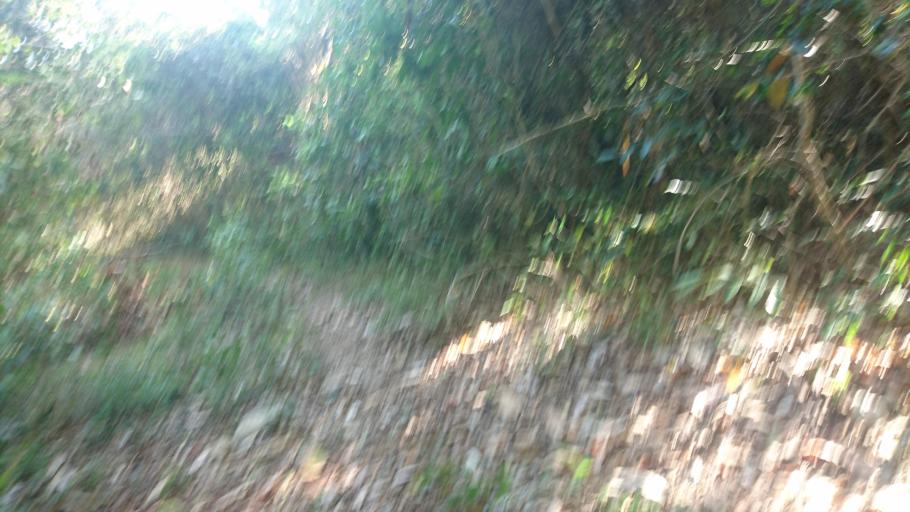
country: CU
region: Artemisa
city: Soroa
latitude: 22.8313
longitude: -82.9205
